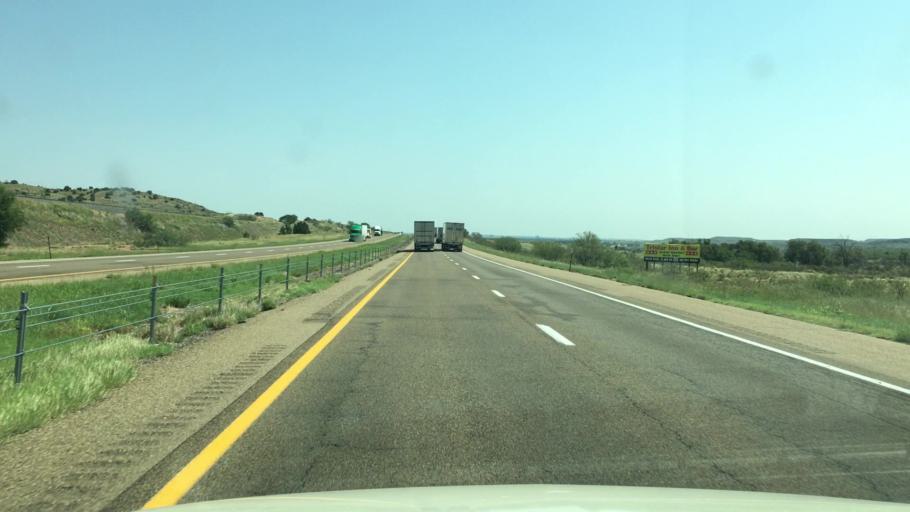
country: US
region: New Mexico
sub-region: Quay County
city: Tucumcari
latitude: 35.1358
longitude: -103.8333
